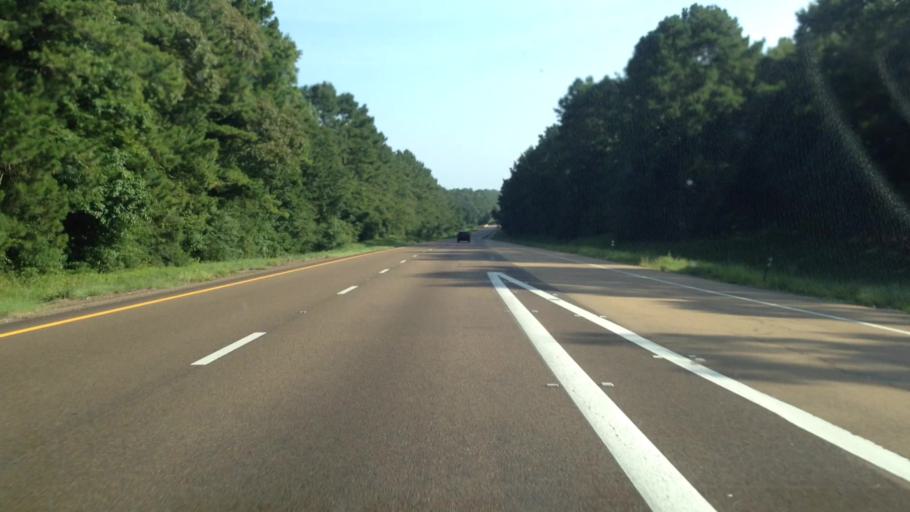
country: US
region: Mississippi
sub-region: Pike County
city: Summit
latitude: 31.3520
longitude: -90.4789
